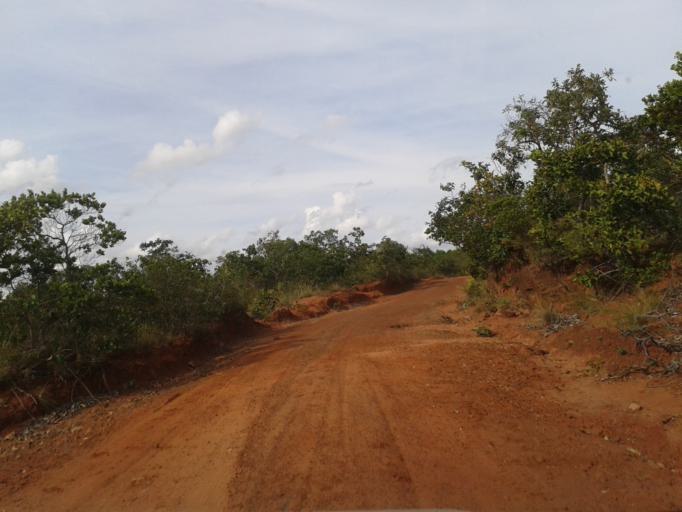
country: BR
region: Minas Gerais
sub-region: Campina Verde
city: Campina Verde
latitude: -19.4516
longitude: -49.6064
